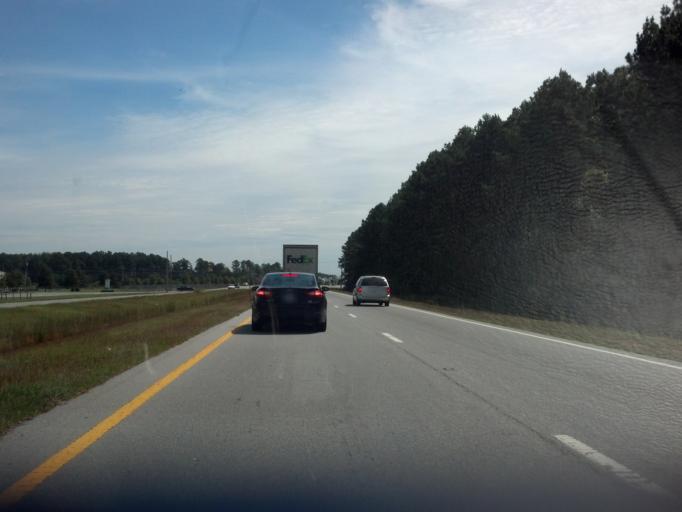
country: US
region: North Carolina
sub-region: Pitt County
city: Greenville
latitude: 35.6578
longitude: -77.3568
